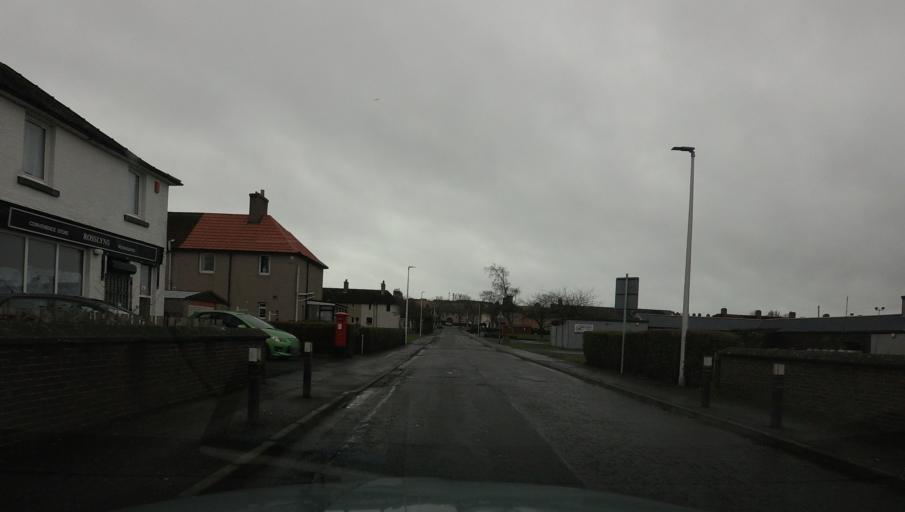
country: GB
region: Scotland
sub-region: Fife
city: Inverkeithing
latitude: 56.0388
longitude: -3.4099
